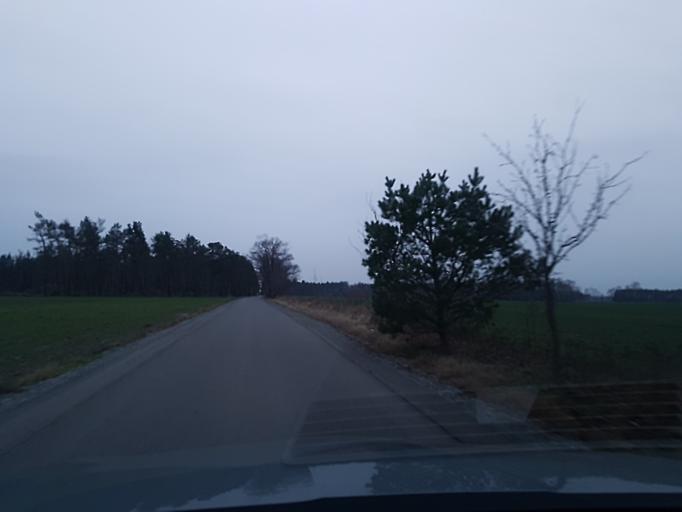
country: DE
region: Brandenburg
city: Schonewalde
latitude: 51.6496
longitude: 13.6197
